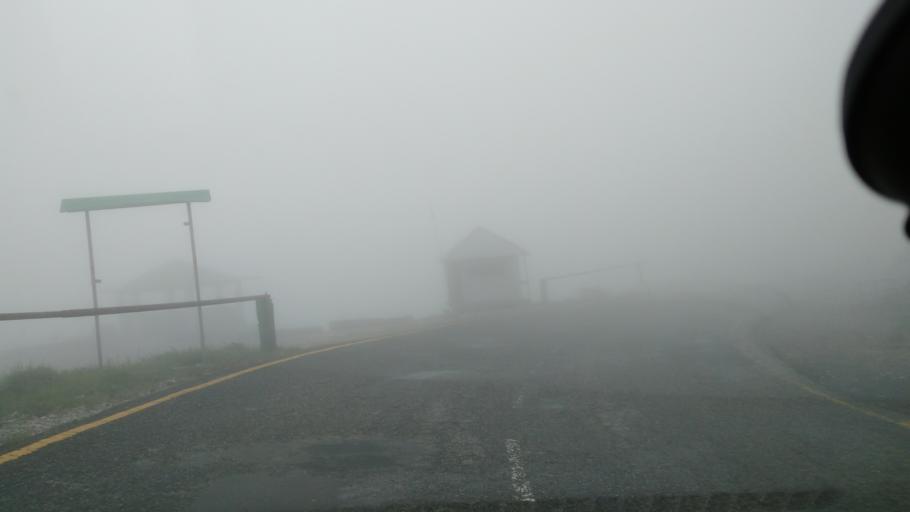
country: IN
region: Meghalaya
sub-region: East Khasi Hills
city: Cherrapunji
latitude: 25.3121
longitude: 91.7304
